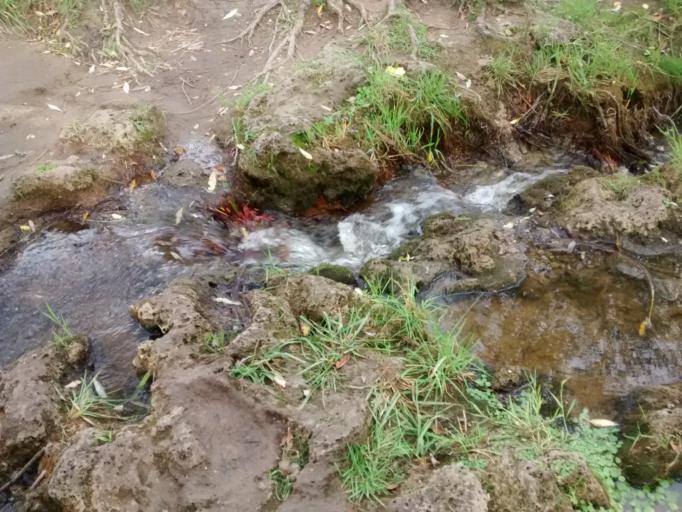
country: AR
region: Buenos Aires
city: Necochea
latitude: -38.4601
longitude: -58.7611
